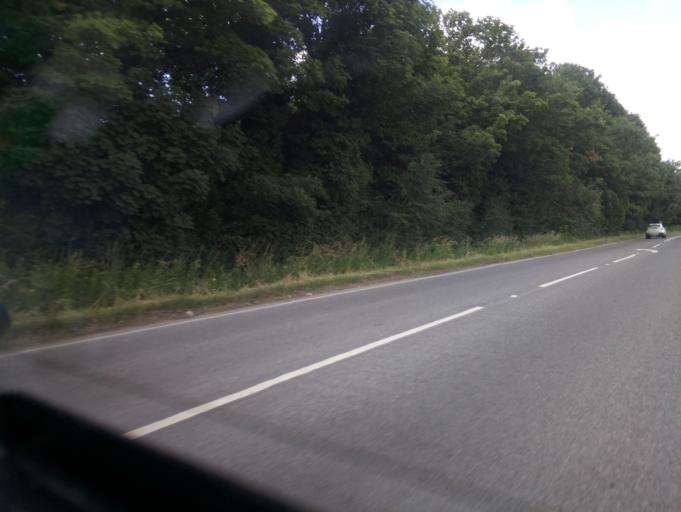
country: GB
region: England
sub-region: Nottinghamshire
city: Ruddington
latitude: 52.8546
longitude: -1.1367
